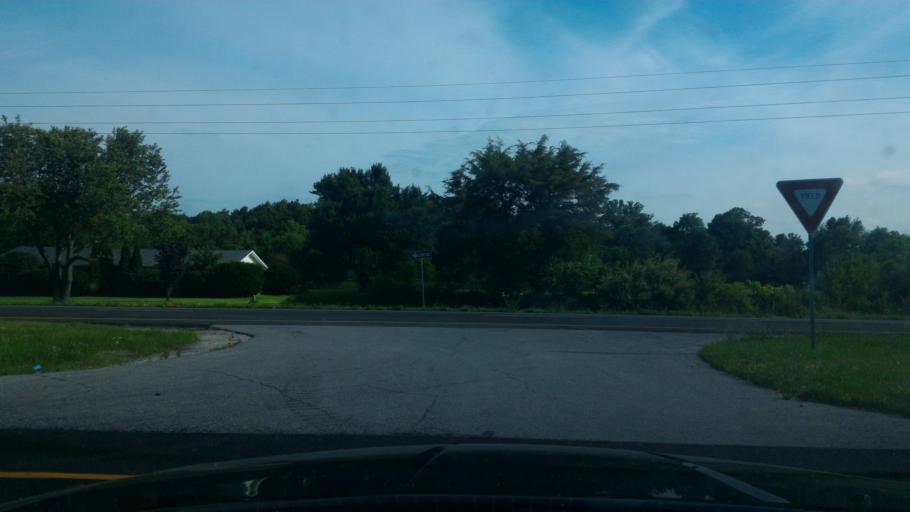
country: US
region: Indiana
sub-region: Tippecanoe County
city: West Lafayette
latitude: 40.4678
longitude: -86.9913
